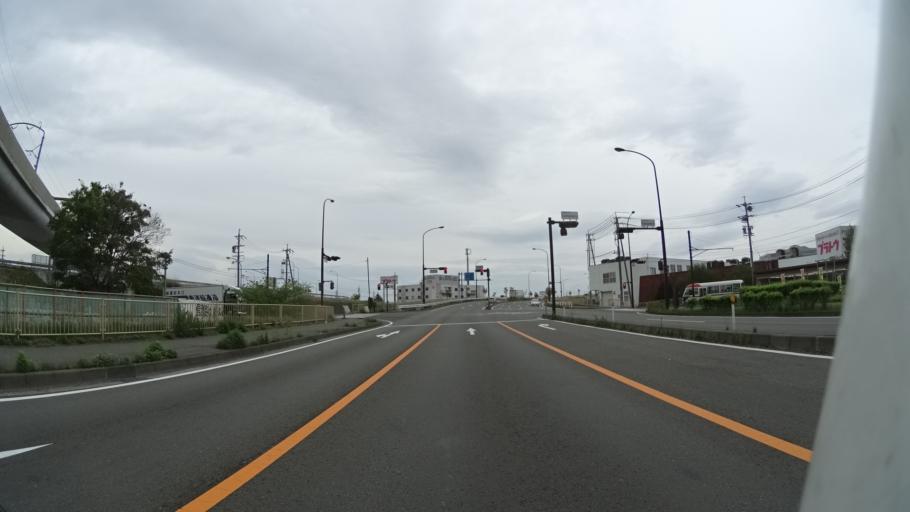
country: JP
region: Nagano
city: Nagano-shi
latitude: 36.5483
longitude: 138.1309
